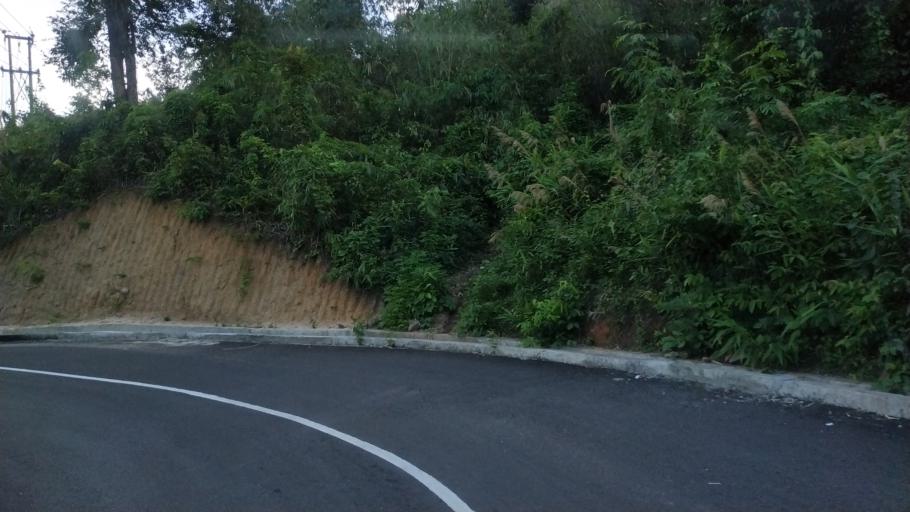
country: MM
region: Mon
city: Kyaikto
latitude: 17.4427
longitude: 97.0976
